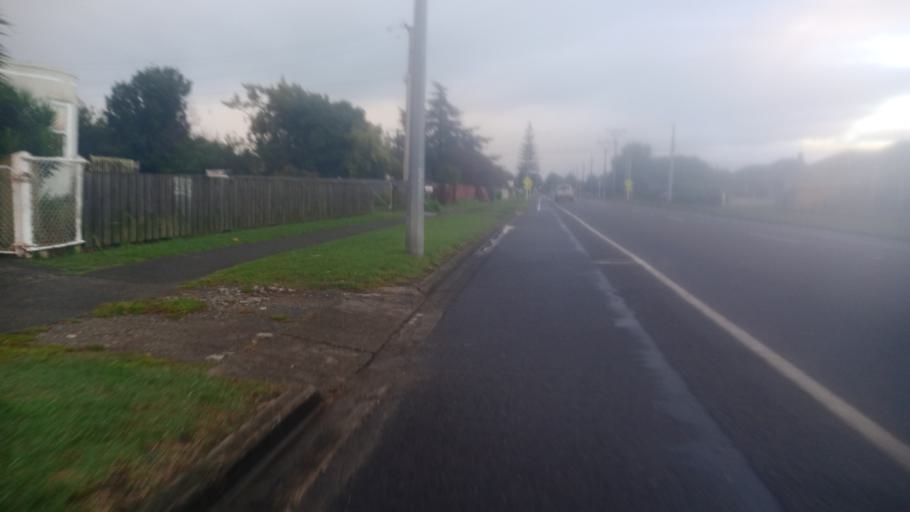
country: NZ
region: Gisborne
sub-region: Gisborne District
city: Gisborne
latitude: -38.6589
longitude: 177.9948
